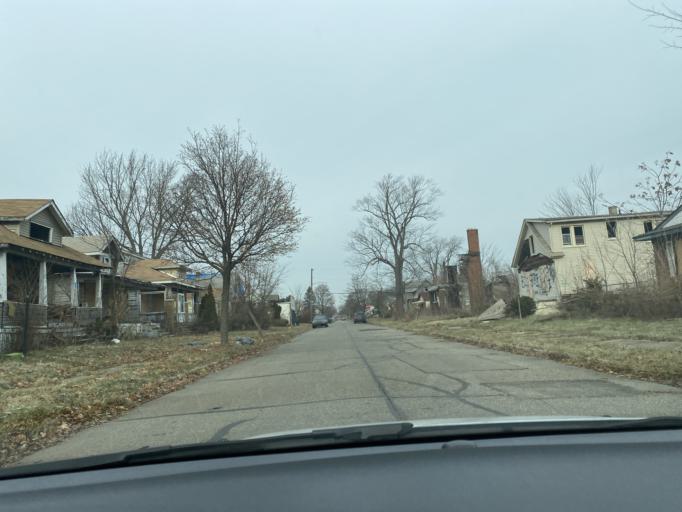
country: US
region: Michigan
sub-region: Wayne County
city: Highland Park
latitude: 42.3737
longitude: -83.1340
